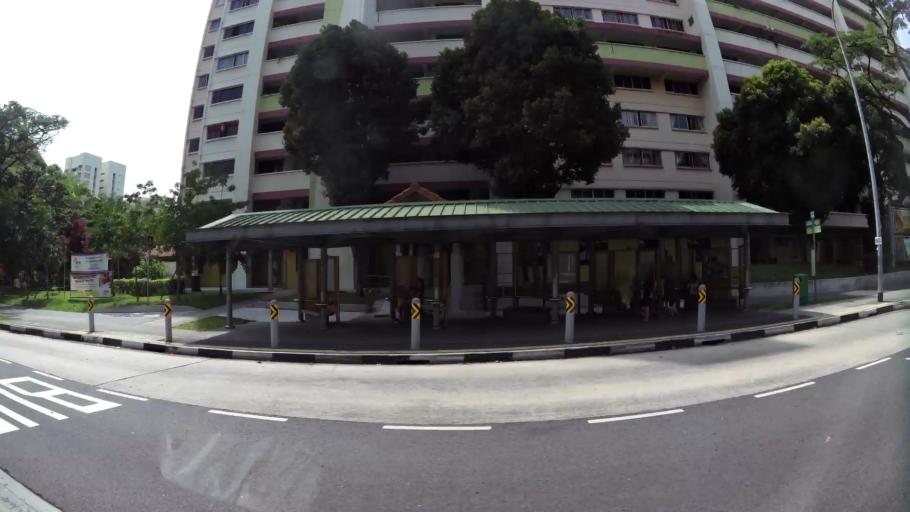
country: MY
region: Johor
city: Johor Bahru
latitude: 1.3499
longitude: 103.7274
